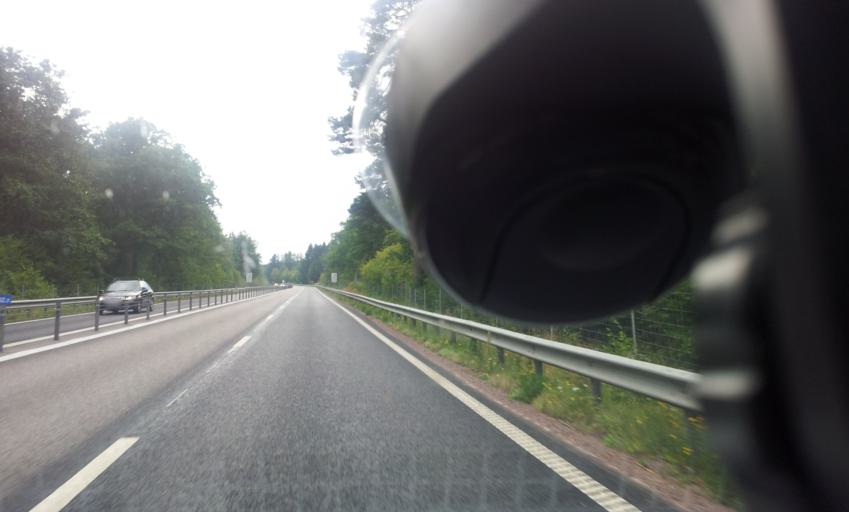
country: SE
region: Kalmar
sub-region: Monsteras Kommun
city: Timmernabben
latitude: 56.9369
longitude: 16.3872
